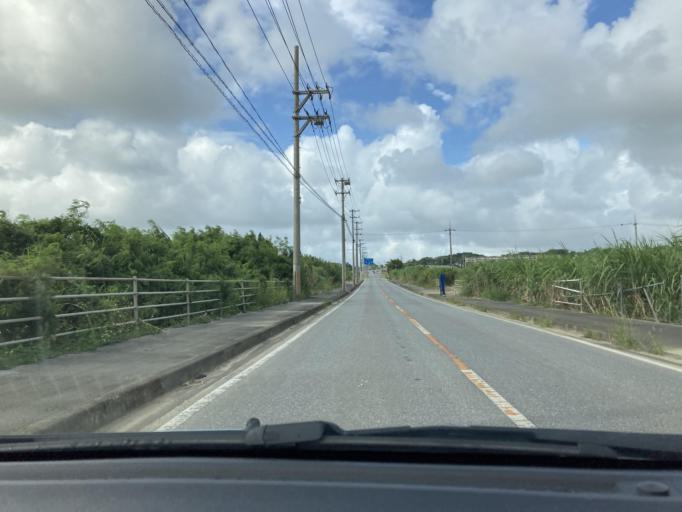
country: JP
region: Okinawa
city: Itoman
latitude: 26.1129
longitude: 127.6922
